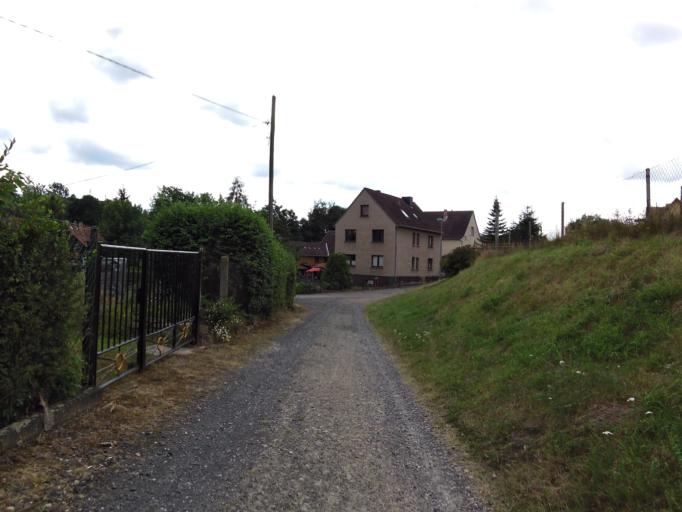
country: DE
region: Thuringia
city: Bad Salzungen
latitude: 50.8119
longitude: 10.2510
